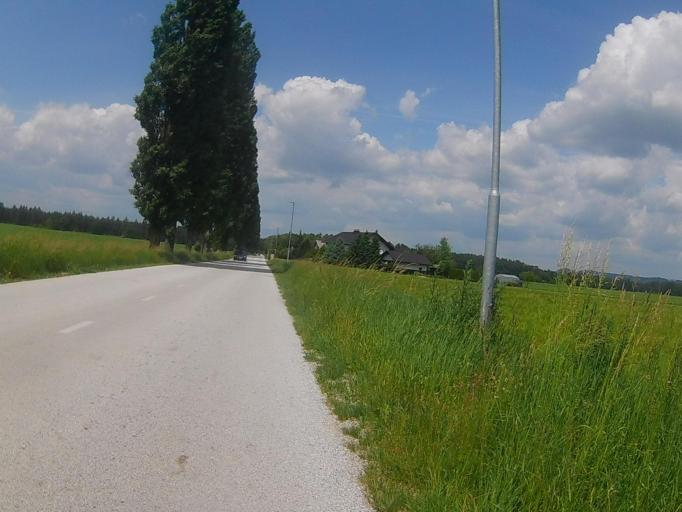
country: SI
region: Kidricevo
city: Kidricevo
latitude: 46.4283
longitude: 15.7814
